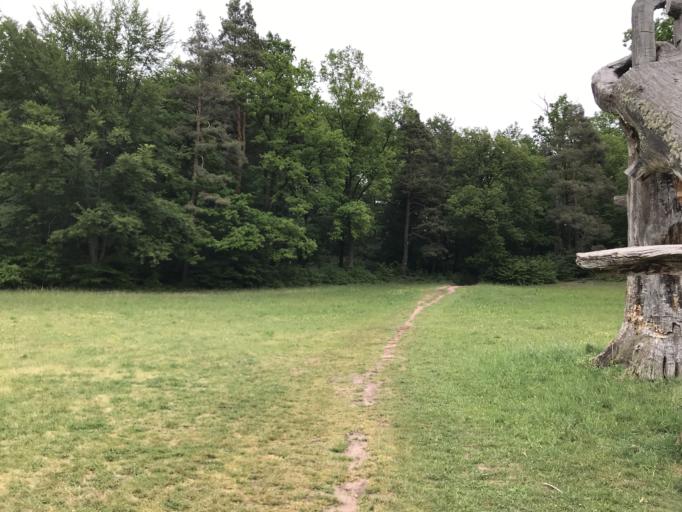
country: DE
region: Baden-Wuerttemberg
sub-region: Regierungsbezirk Stuttgart
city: Gerlingen
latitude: 48.7746
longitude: 9.0861
